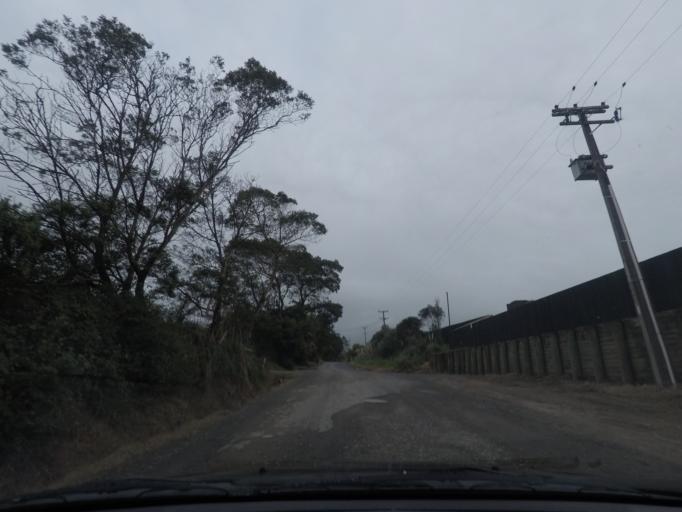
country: NZ
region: Auckland
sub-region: Auckland
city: Muriwai Beach
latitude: -36.7569
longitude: 174.5753
